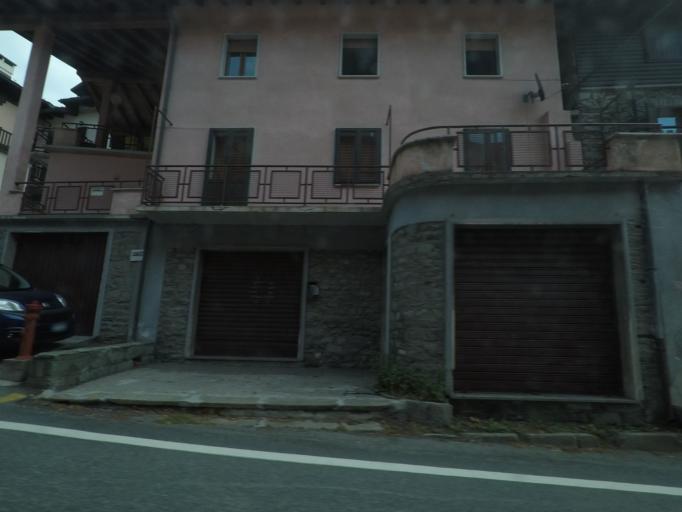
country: IT
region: Aosta Valley
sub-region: Valle d'Aosta
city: Antey-Saint-Andre
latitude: 45.8031
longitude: 7.5888
